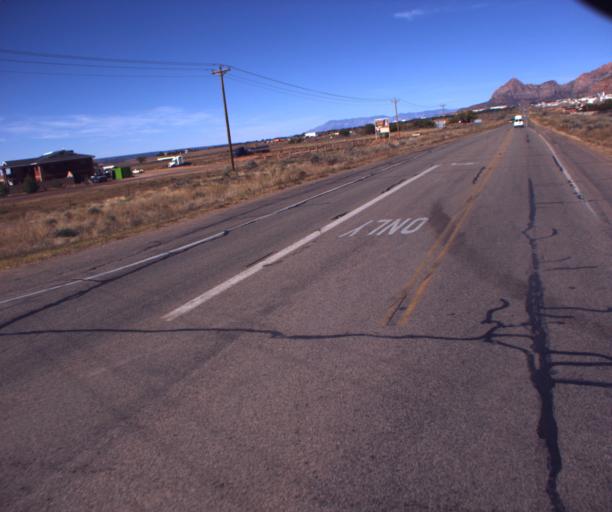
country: US
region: Arizona
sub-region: Mohave County
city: Colorado City
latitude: 36.9833
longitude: -112.9853
